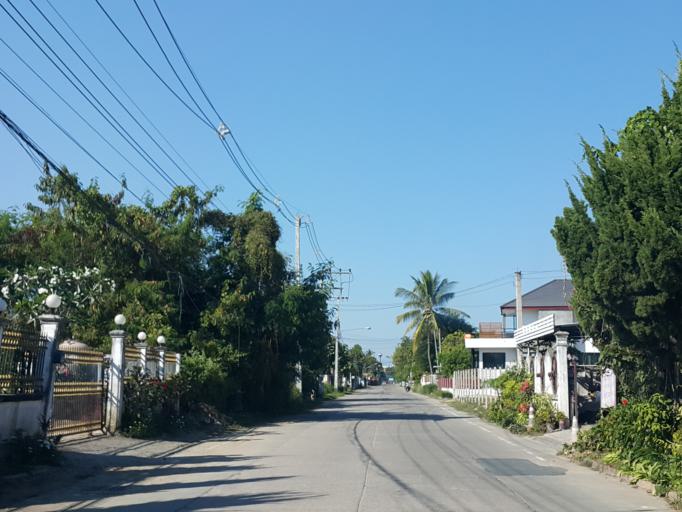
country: TH
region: Chiang Mai
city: San Sai
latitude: 18.8803
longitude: 99.0130
